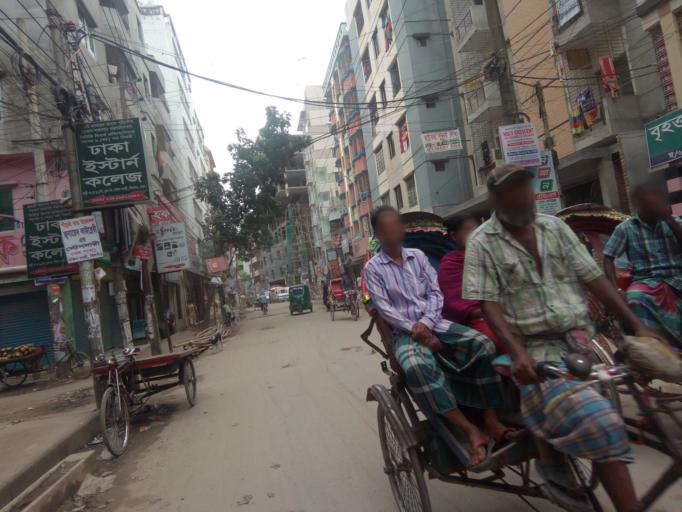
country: BD
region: Dhaka
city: Paltan
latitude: 23.7506
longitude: 90.4411
